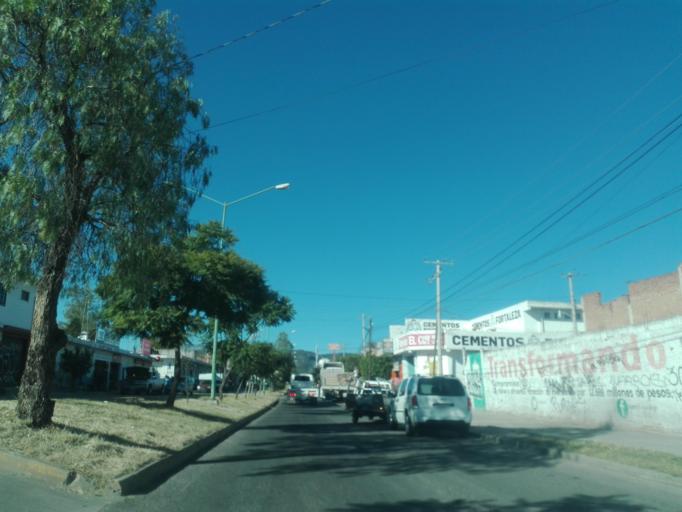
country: MX
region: Guanajuato
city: Leon
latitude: 21.1757
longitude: -101.6759
